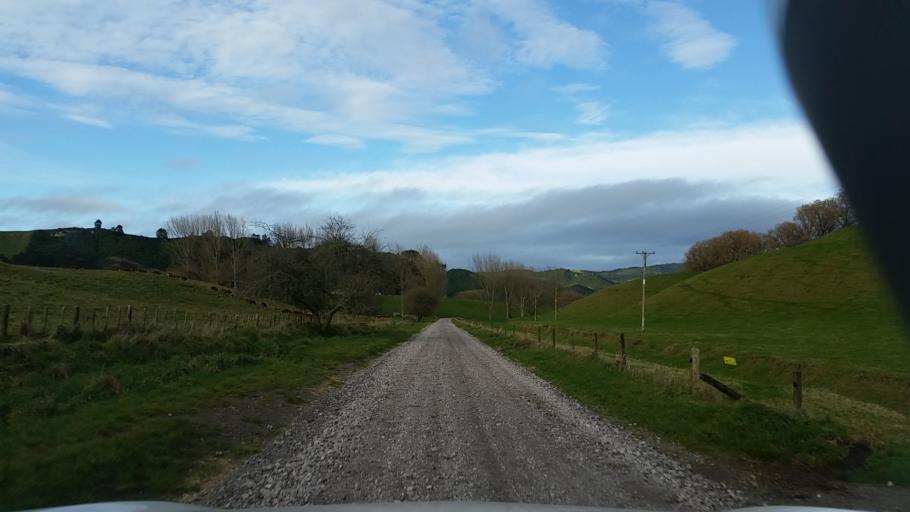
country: NZ
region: Bay of Plenty
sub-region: Rotorua District
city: Rotorua
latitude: -38.3133
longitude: 176.3022
